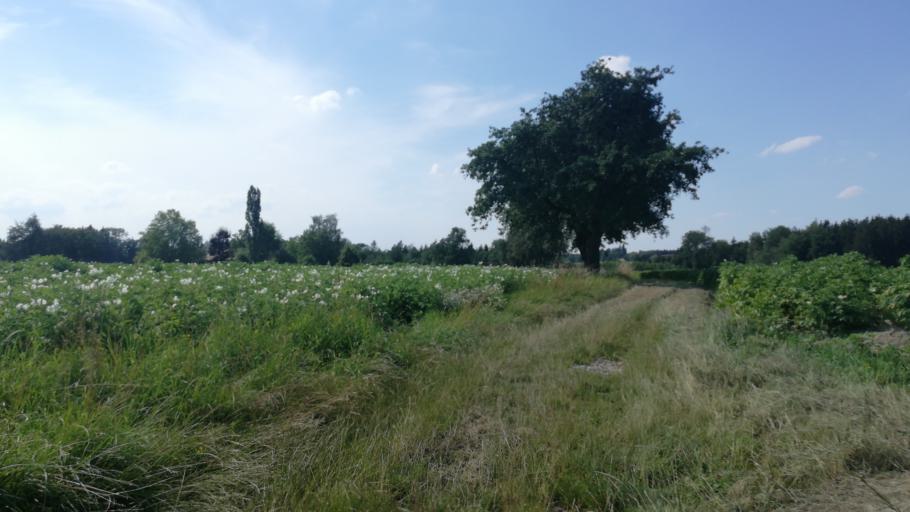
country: AT
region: Upper Austria
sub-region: Wels-Land
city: Gunskirchen
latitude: 48.1637
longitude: 13.9251
